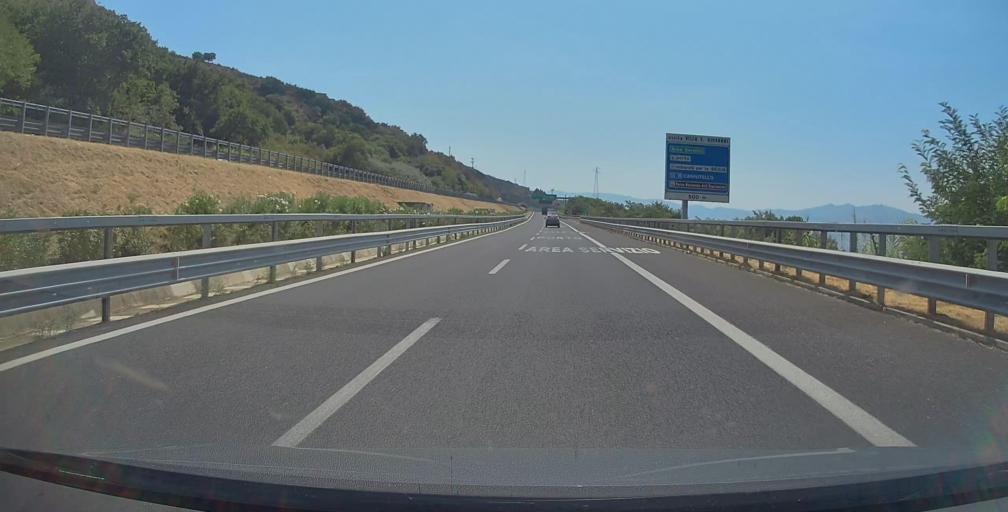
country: IT
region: Calabria
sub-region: Provincia di Reggio Calabria
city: Villa San Giovanni
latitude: 38.2305
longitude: 15.6600
